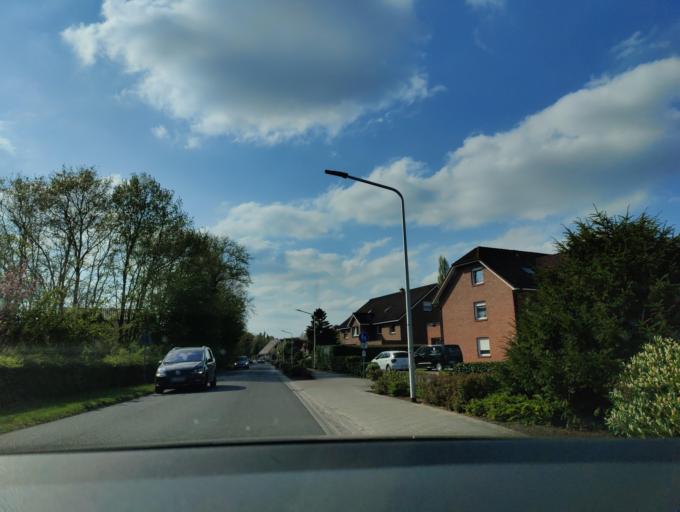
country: DE
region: Lower Saxony
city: Emsburen
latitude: 52.3868
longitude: 7.3019
